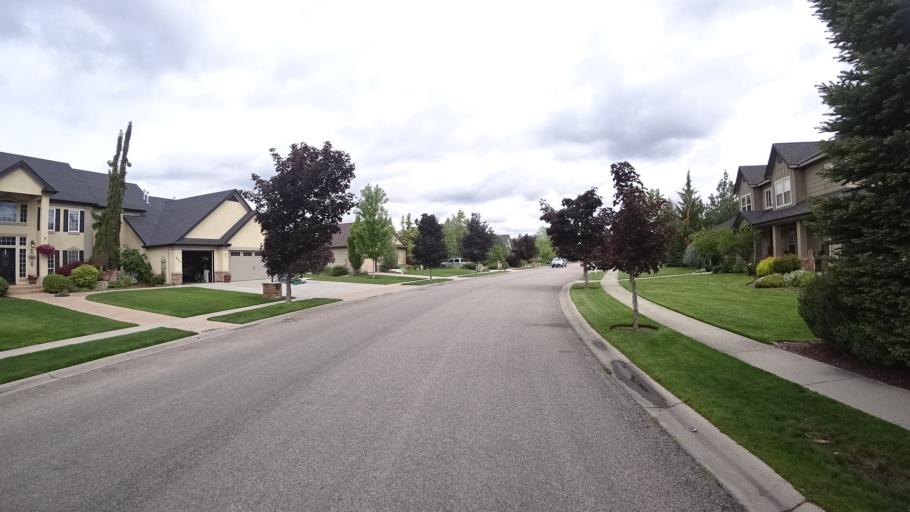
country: US
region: Idaho
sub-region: Ada County
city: Eagle
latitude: 43.6807
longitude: -116.3603
